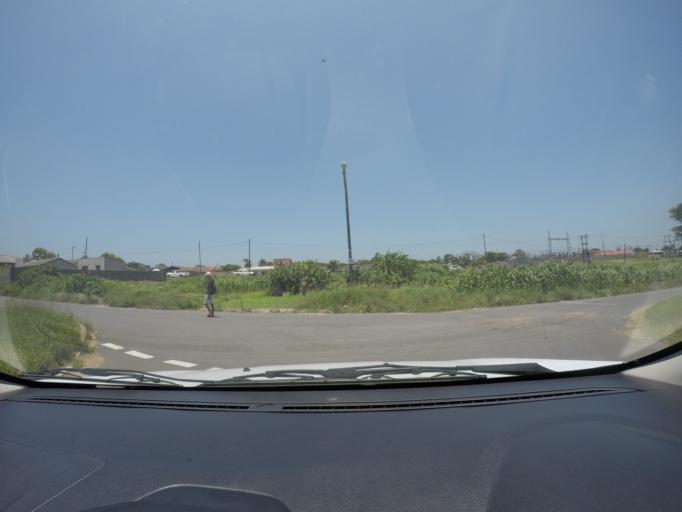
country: ZA
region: KwaZulu-Natal
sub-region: uThungulu District Municipality
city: eSikhawini
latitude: -28.8843
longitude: 31.9010
